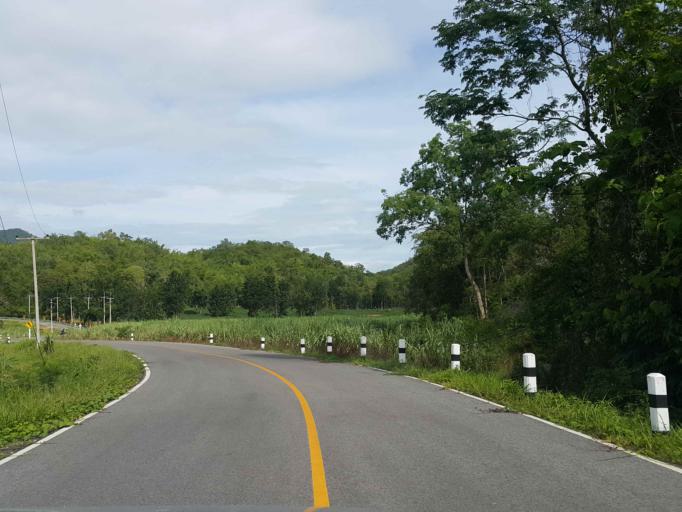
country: TH
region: Sukhothai
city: Thung Saliam
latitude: 17.2387
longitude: 99.5003
